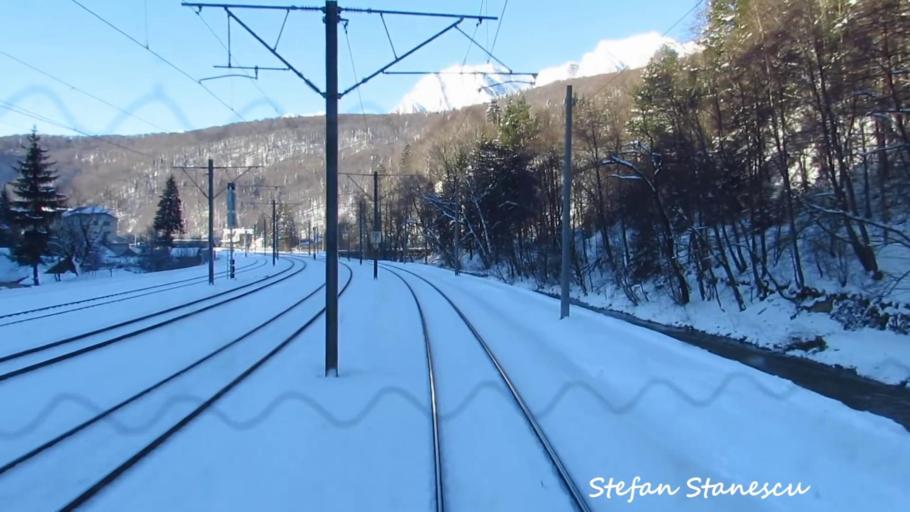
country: RO
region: Prahova
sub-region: Oras Azuga
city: Azuga
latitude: 45.4490
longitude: 25.5567
